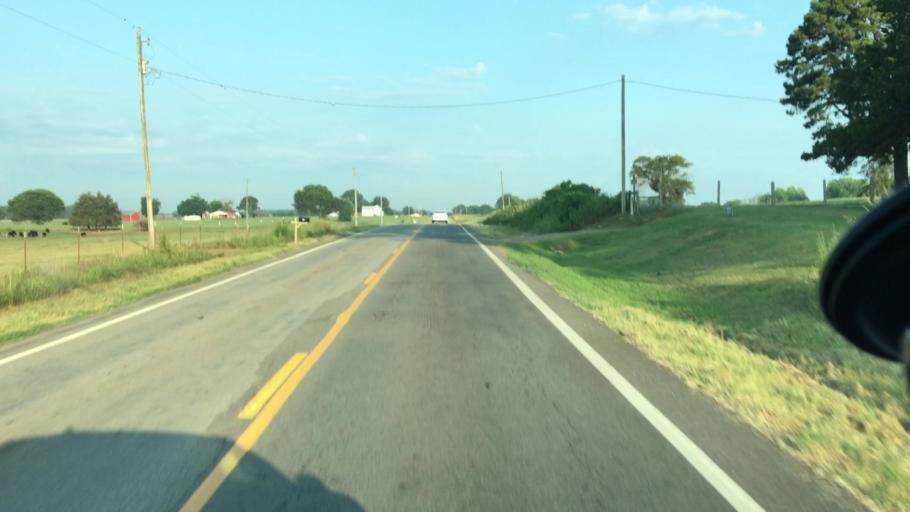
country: US
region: Arkansas
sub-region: Johnson County
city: Clarksville
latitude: 35.3787
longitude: -93.5361
